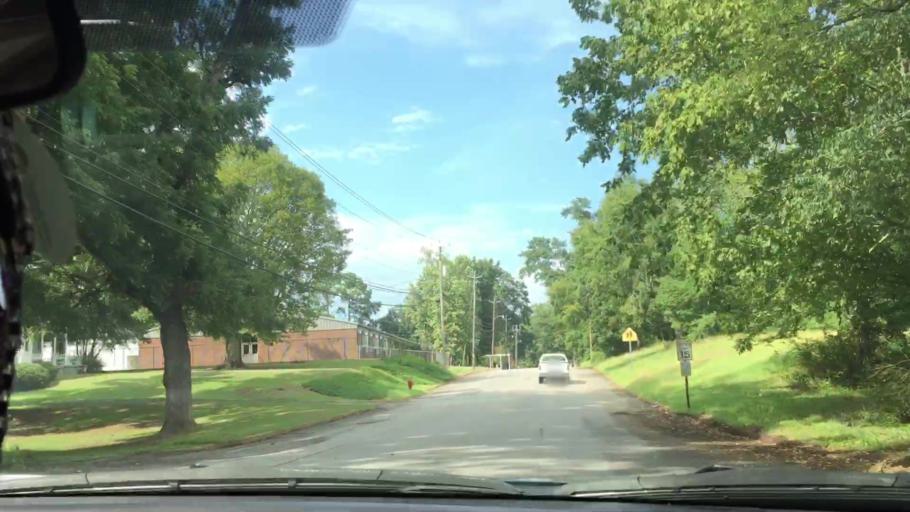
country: US
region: Alabama
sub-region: Hale County
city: Greensboro
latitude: 32.7009
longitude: -87.5997
